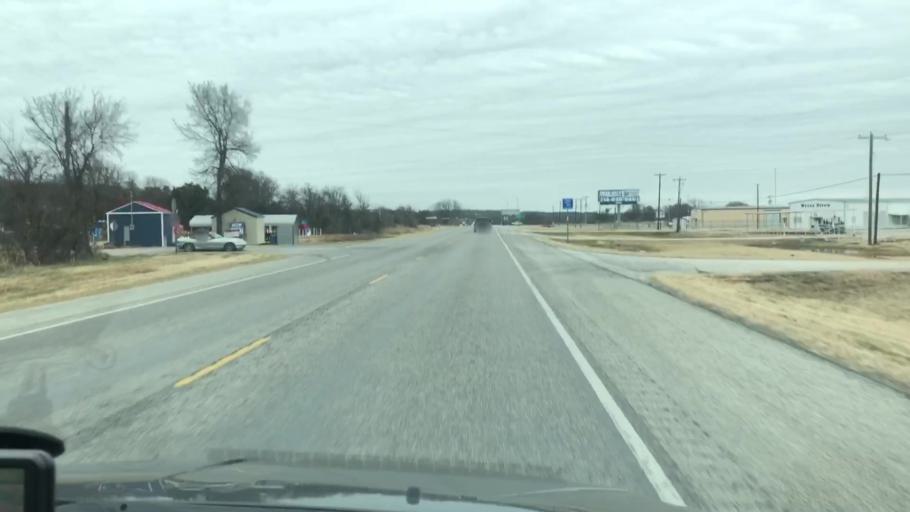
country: US
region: Texas
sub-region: Palo Pinto County
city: Mineral Wells
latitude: 32.8514
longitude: -98.0966
